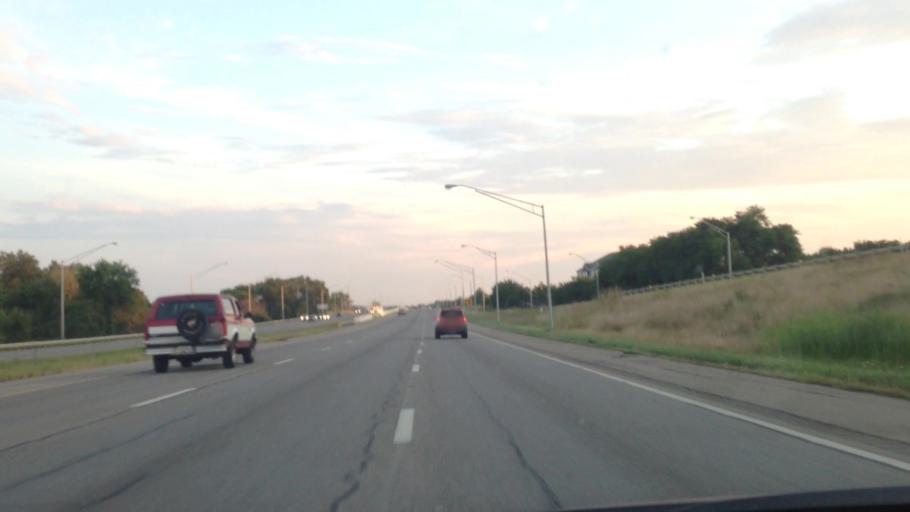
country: US
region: Ohio
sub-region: Stark County
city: Greentown
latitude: 40.9139
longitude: -81.4272
